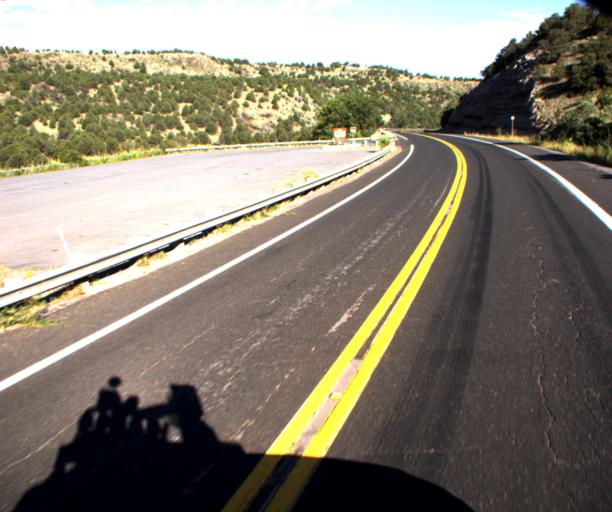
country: US
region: Arizona
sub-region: Apache County
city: Eagar
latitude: 34.0604
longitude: -109.1939
